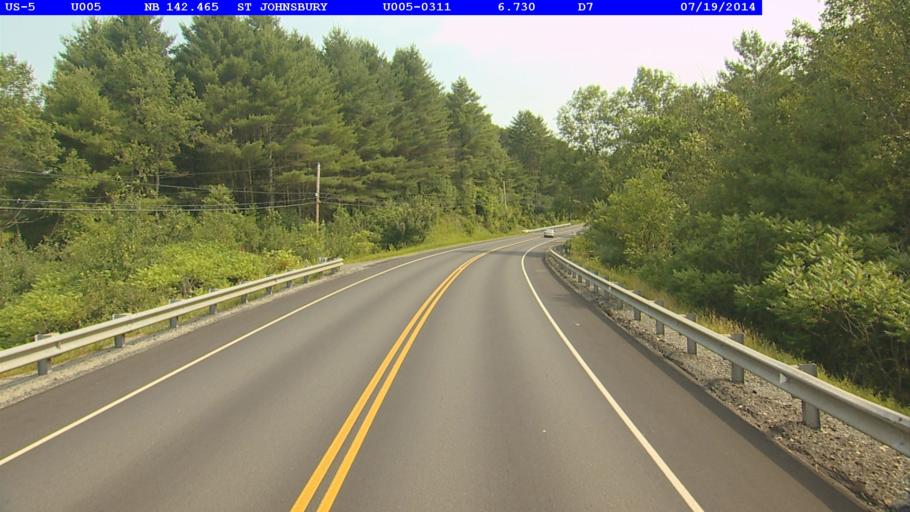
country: US
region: Vermont
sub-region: Caledonia County
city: Lyndon
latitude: 44.4863
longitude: -72.0106
